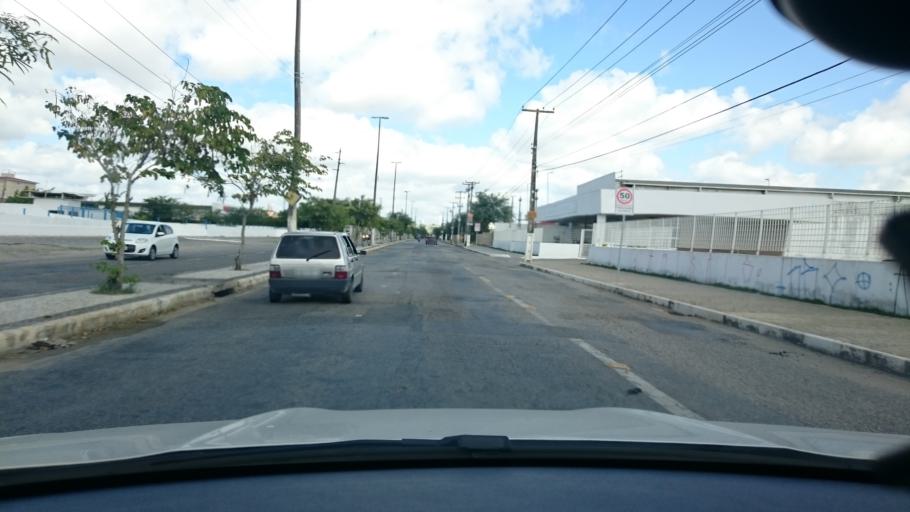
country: BR
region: Paraiba
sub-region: Campina Grande
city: Campina Grande
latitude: -7.2342
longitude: -35.9166
